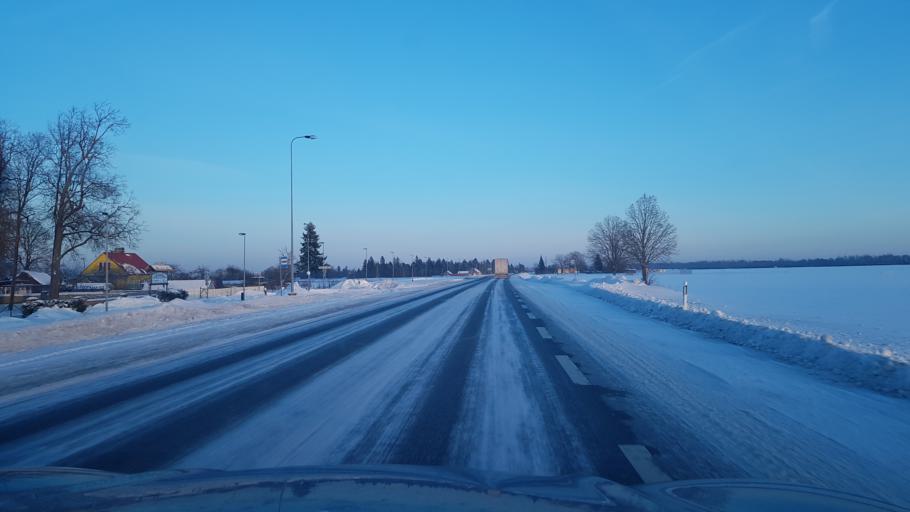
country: EE
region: Ida-Virumaa
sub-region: Narva linn
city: Narva
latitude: 59.3900
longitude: 28.1043
